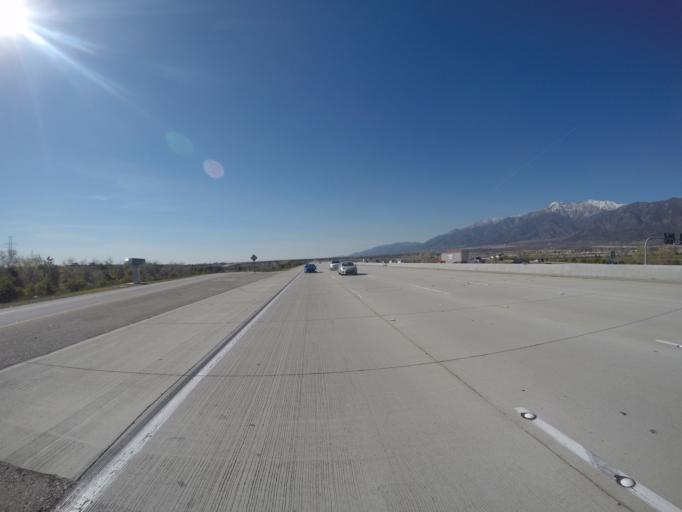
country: US
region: California
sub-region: San Bernardino County
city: Fontana
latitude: 34.1362
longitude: -117.4859
